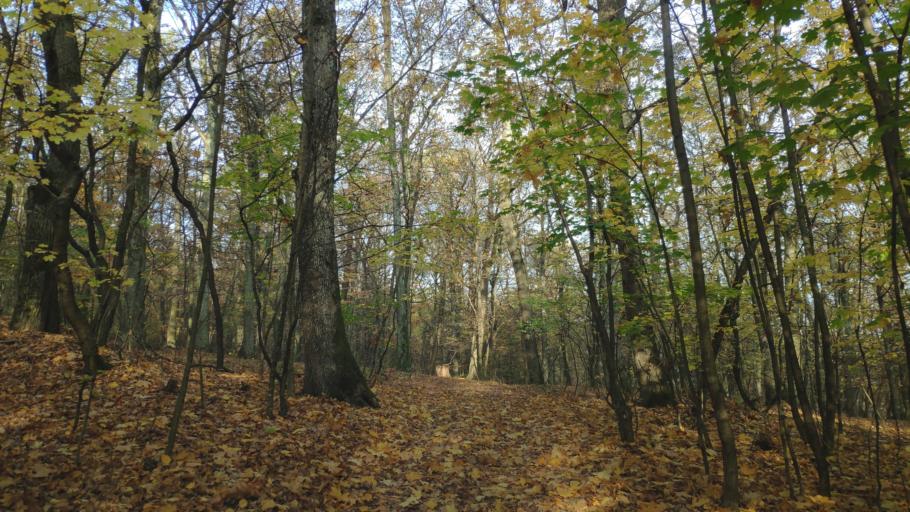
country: SK
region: Kosicky
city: Kosice
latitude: 48.7461
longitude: 21.2256
